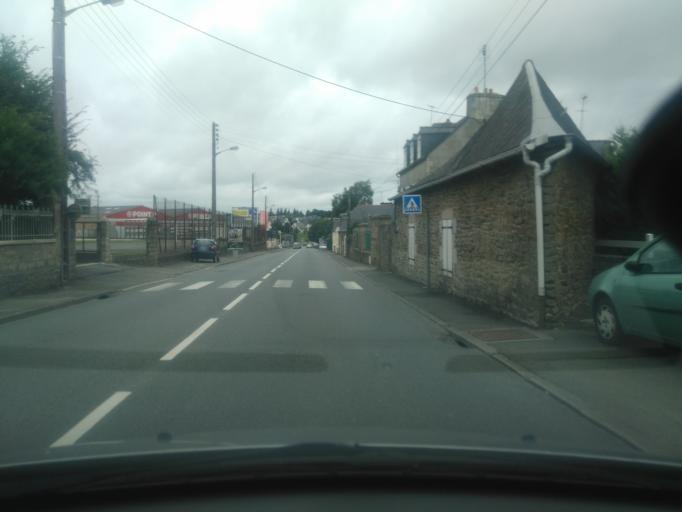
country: FR
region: Brittany
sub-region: Departement des Cotes-d'Armor
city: Lehon
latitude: 48.4581
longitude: -2.0548
